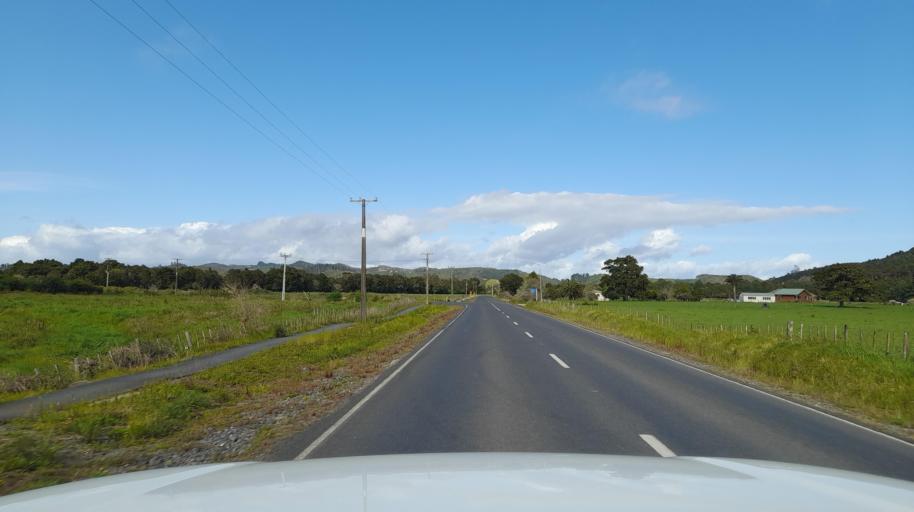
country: NZ
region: Northland
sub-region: Far North District
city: Moerewa
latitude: -35.4003
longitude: 173.9908
